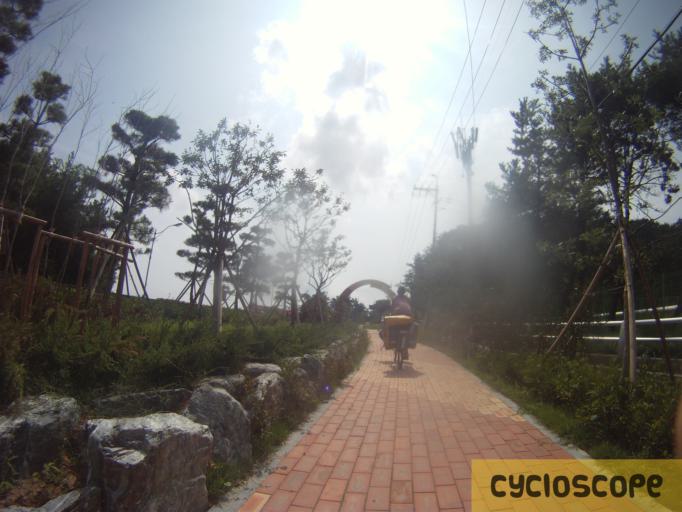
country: KR
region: Busan
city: Kijang
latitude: 35.3142
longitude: 129.2616
